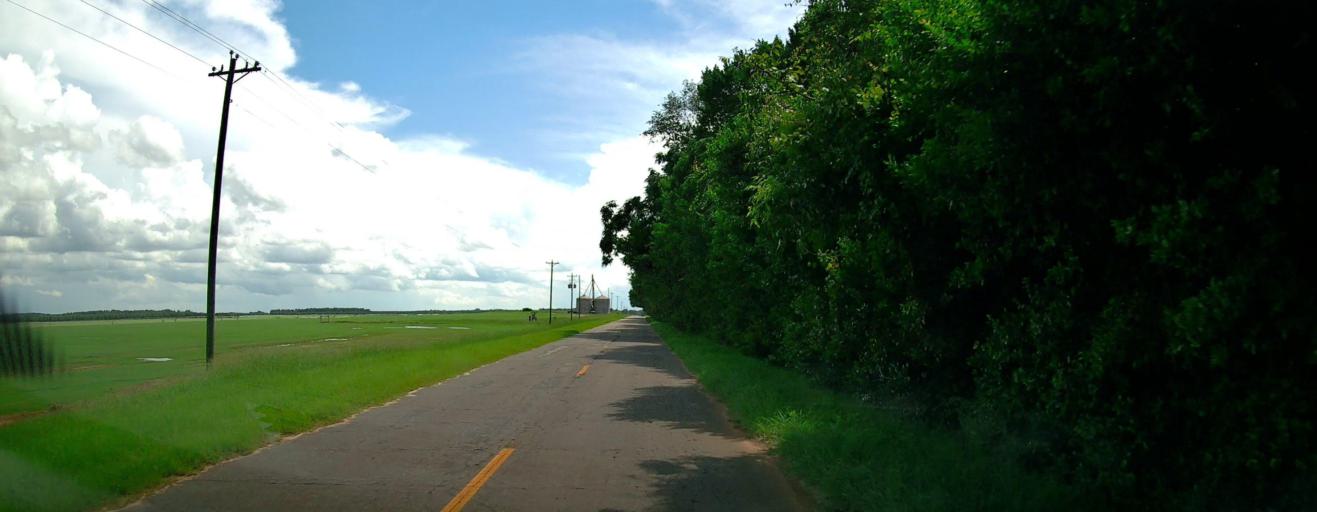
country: US
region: Georgia
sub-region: Macon County
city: Marshallville
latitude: 32.4420
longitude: -84.0005
